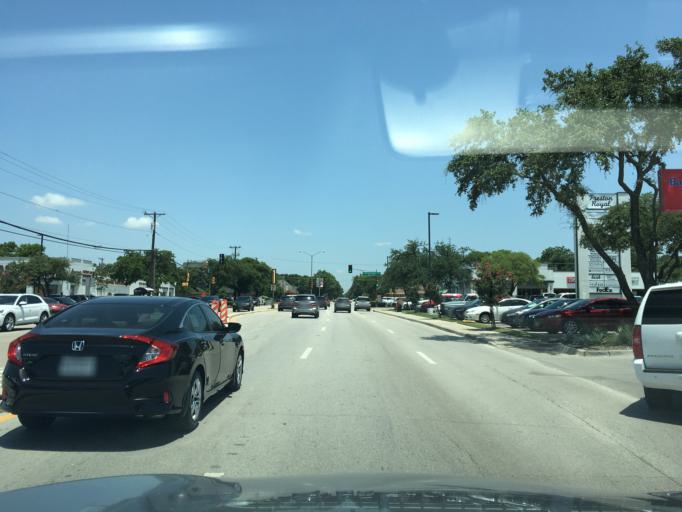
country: US
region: Texas
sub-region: Dallas County
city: University Park
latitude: 32.8953
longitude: -96.8039
